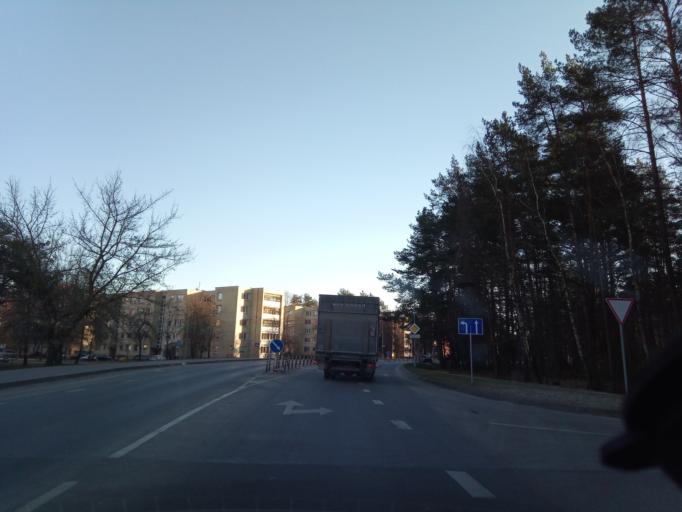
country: LT
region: Alytaus apskritis
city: Druskininkai
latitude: 54.0253
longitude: 23.9991
